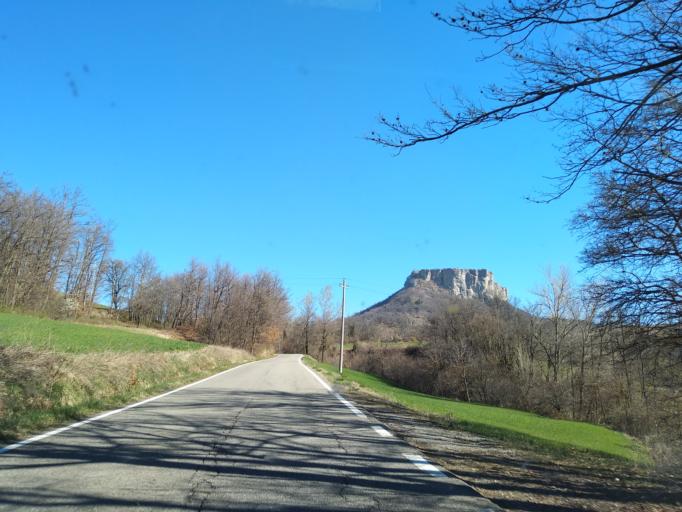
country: IT
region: Emilia-Romagna
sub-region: Provincia di Reggio Emilia
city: Castelnovo ne'Monti
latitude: 44.4085
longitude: 10.3981
